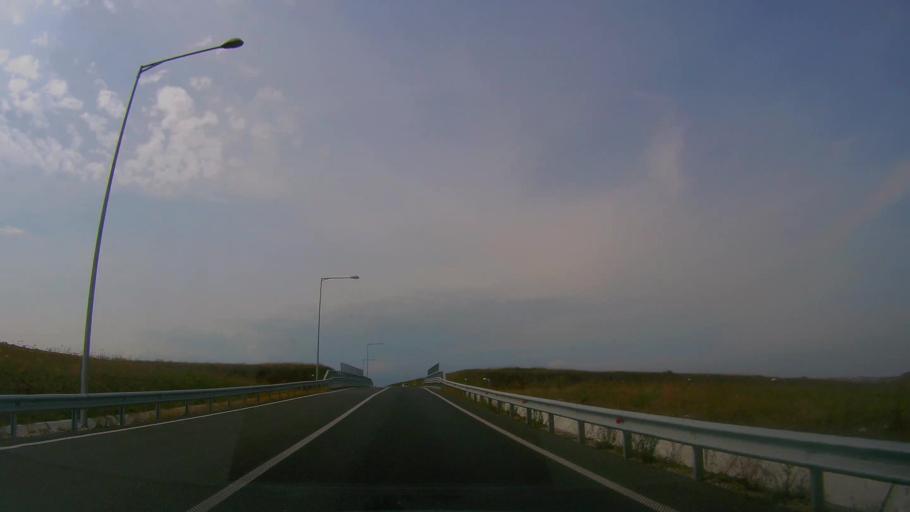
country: RO
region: Cluj
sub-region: Comuna Baciu
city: Mera
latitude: 46.8097
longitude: 23.4212
